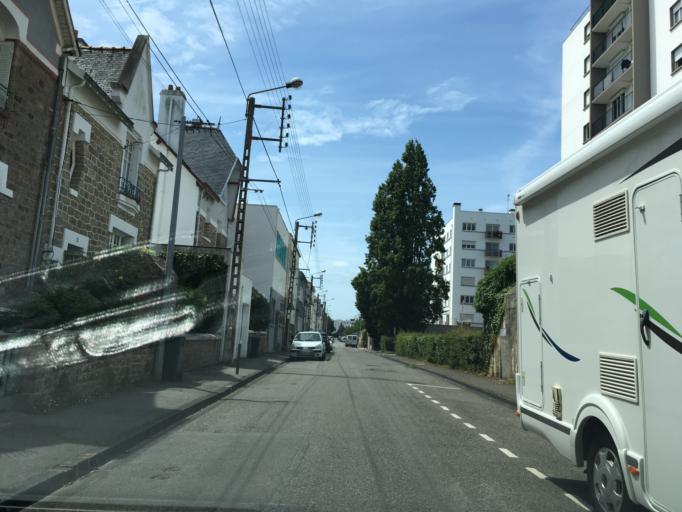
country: FR
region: Brittany
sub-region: Departement du Morbihan
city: Lorient
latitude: 47.7416
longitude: -3.3711
